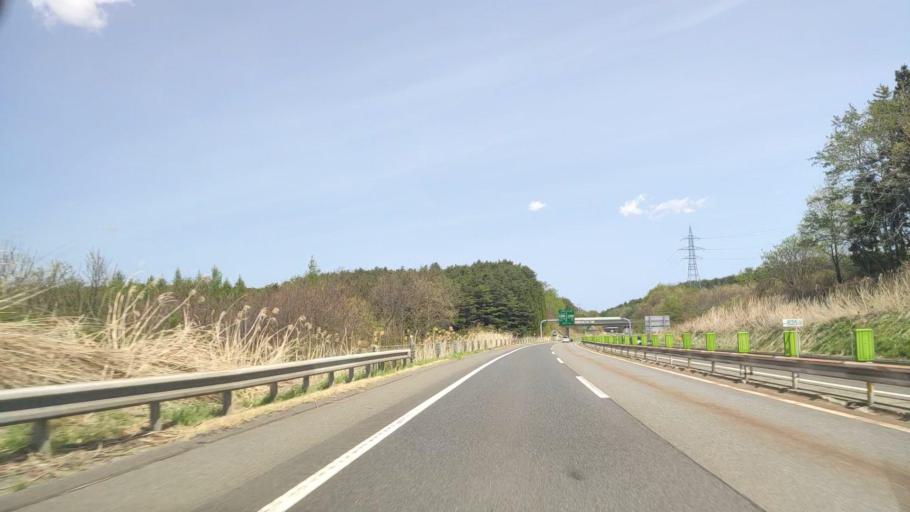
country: JP
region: Aomori
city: Hachinohe
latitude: 40.4469
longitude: 141.4509
